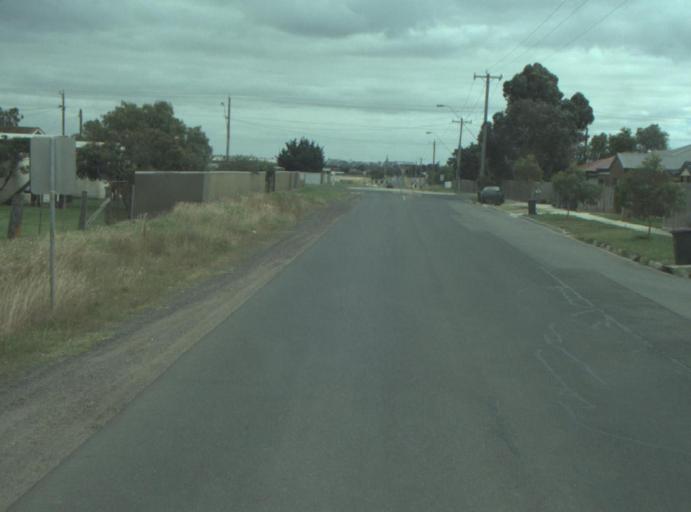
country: AU
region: Victoria
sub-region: Greater Geelong
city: Breakwater
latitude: -38.1979
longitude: 144.3523
